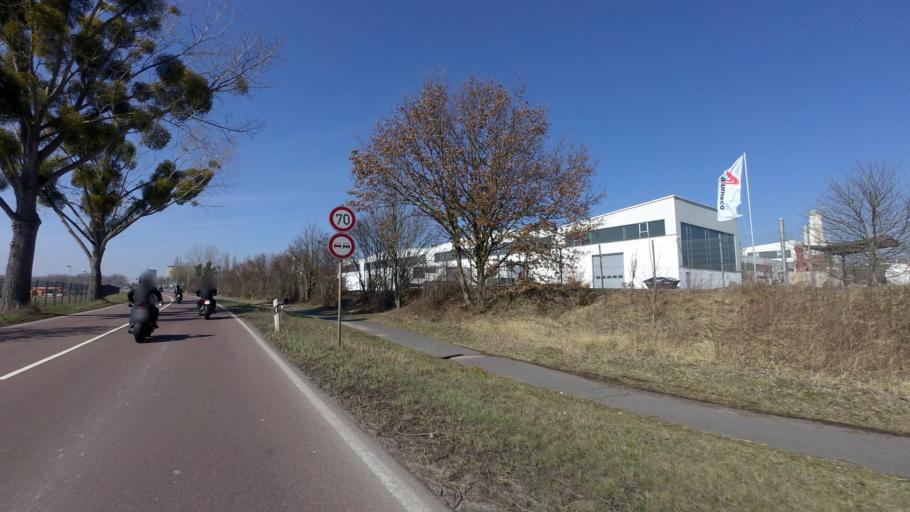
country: DE
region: Saxony-Anhalt
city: Coswig
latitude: 51.8850
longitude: 12.4301
